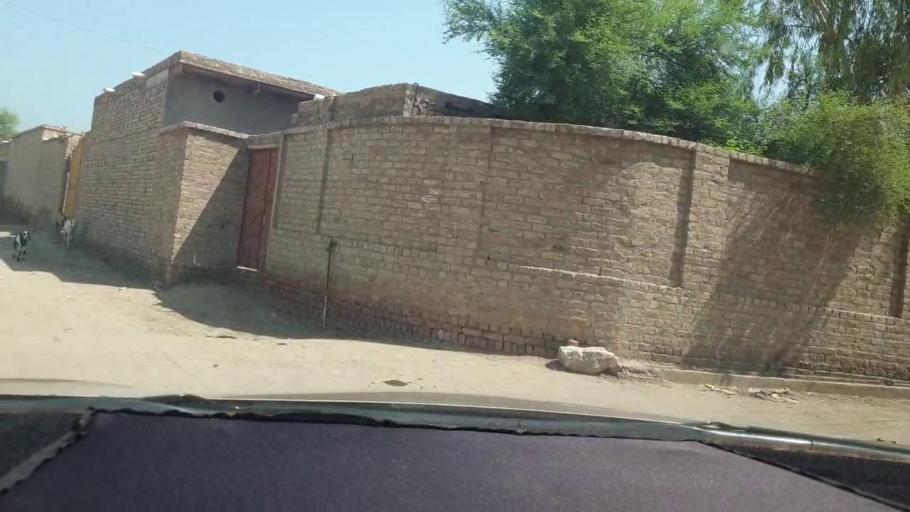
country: PK
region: Sindh
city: Kambar
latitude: 27.5901
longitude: 68.0629
